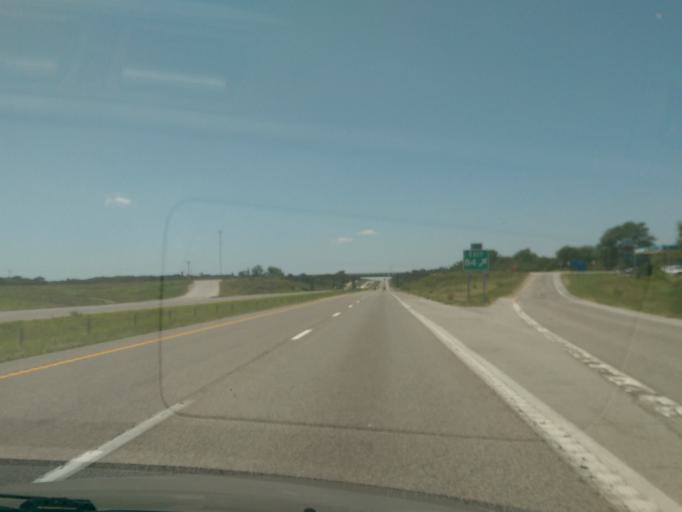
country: US
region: Missouri
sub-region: Saline County
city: Marshall
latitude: 38.9530
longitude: -93.0852
